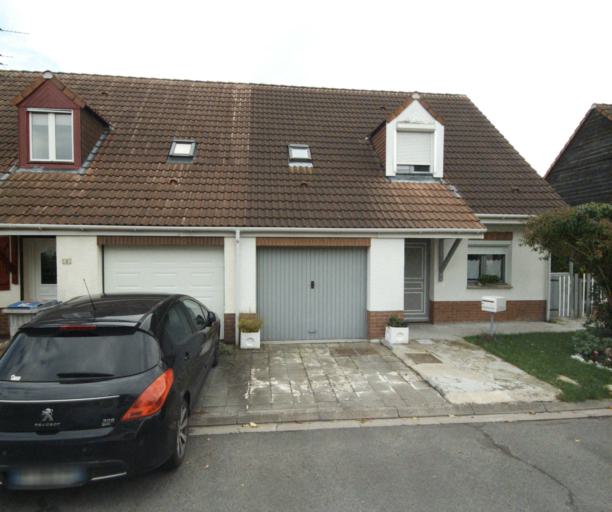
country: FR
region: Nord-Pas-de-Calais
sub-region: Departement du Nord
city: Salome
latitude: 50.5305
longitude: 2.8412
